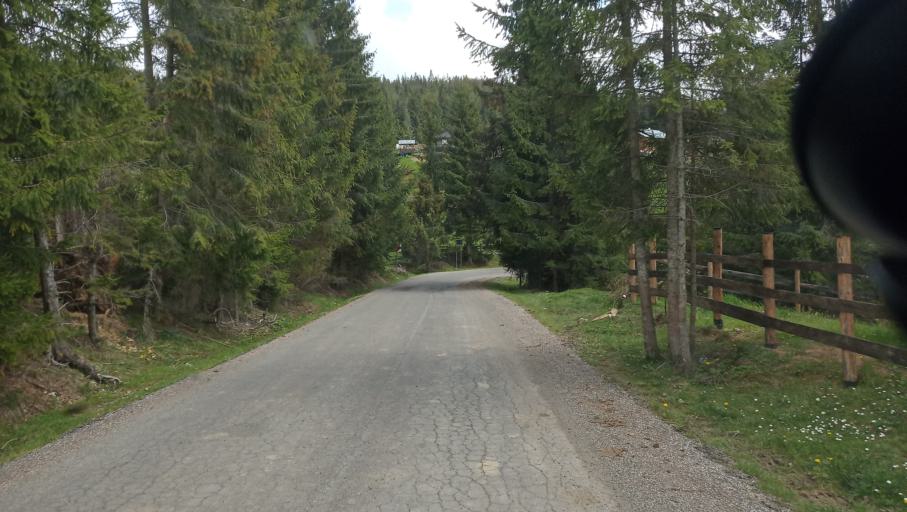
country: RO
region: Alba
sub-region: Comuna Horea
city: Horea
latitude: 46.5495
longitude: 22.8976
